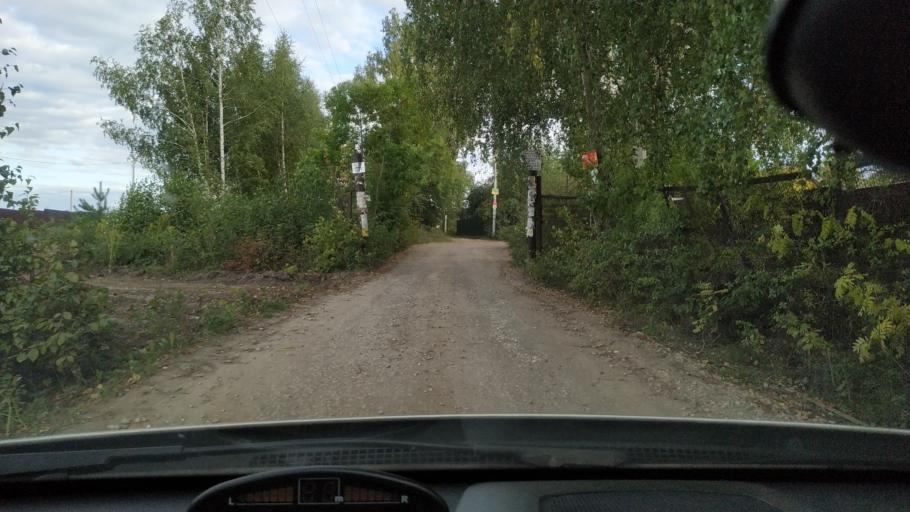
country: RU
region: Rjazan
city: Polyany
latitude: 54.5600
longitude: 39.8779
